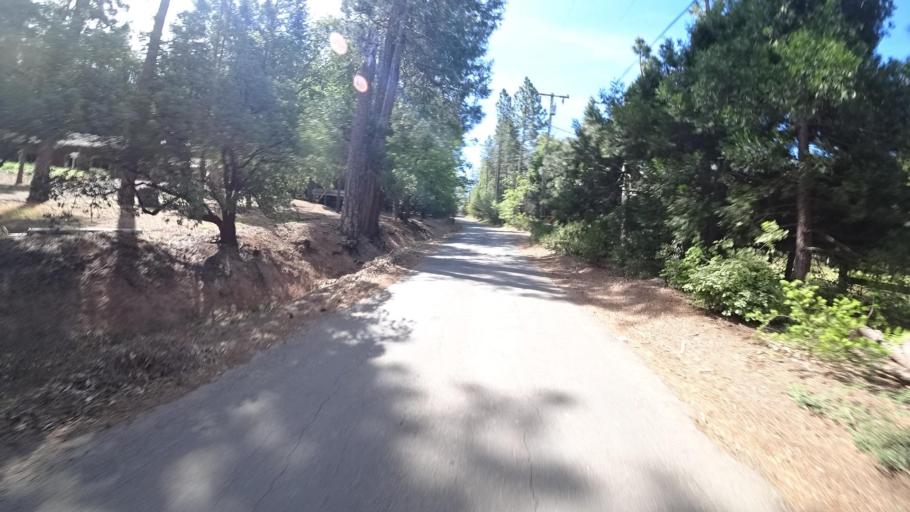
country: US
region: California
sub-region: Lake County
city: Cobb
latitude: 38.8759
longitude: -122.7659
